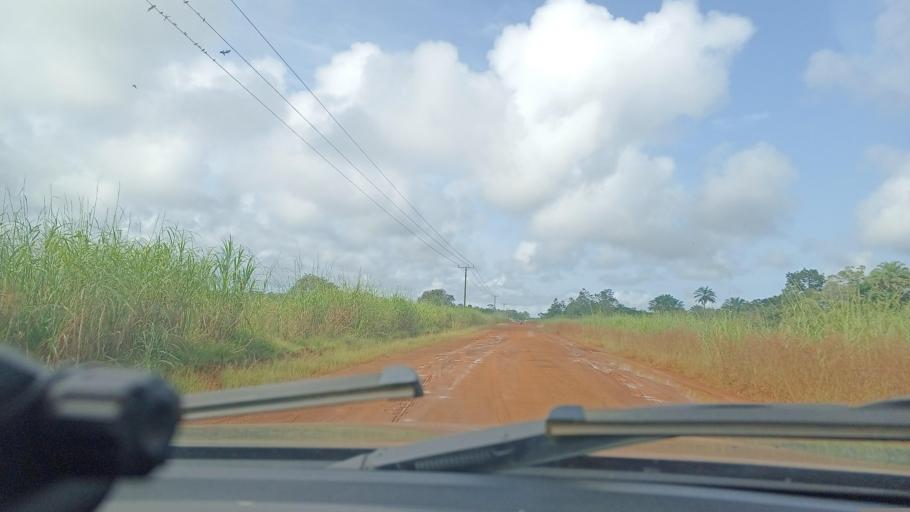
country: LR
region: Grand Cape Mount
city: Robertsport
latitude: 6.6926
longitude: -11.1090
